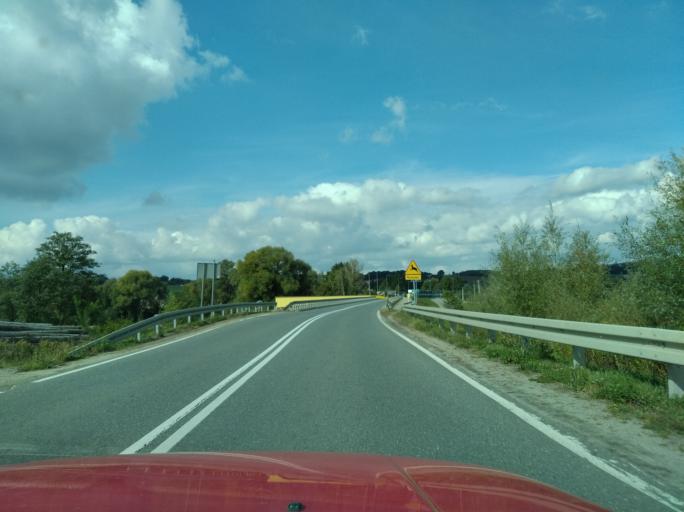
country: PL
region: Subcarpathian Voivodeship
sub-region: Powiat strzyzowski
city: Czudec
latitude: 49.9339
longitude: 21.8176
